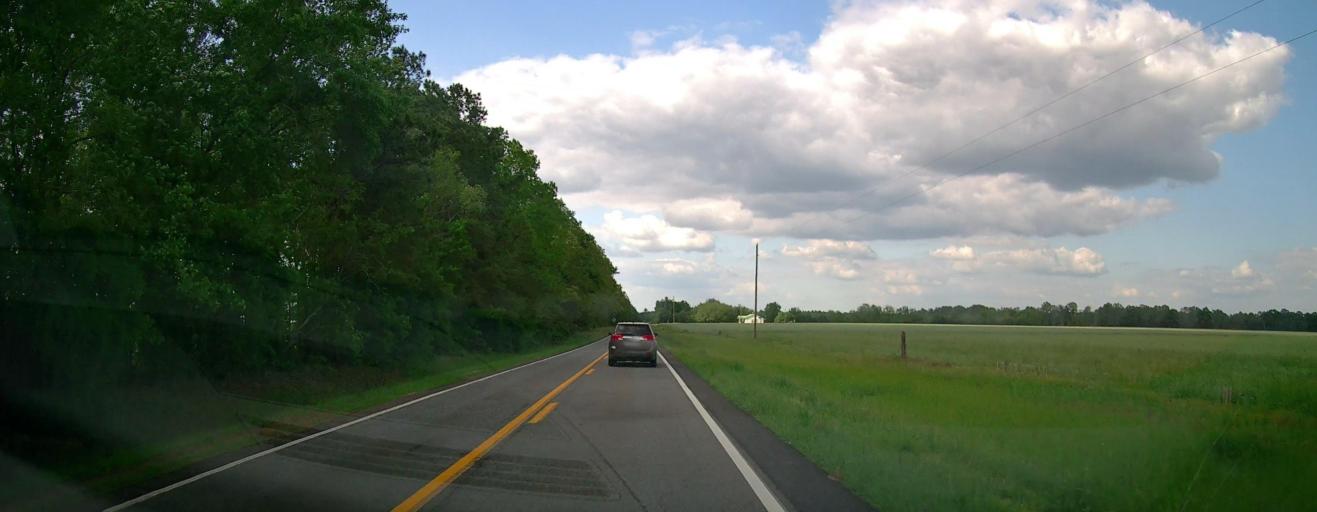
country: US
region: Georgia
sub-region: Laurens County
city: East Dublin
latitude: 32.6526
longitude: -82.8962
